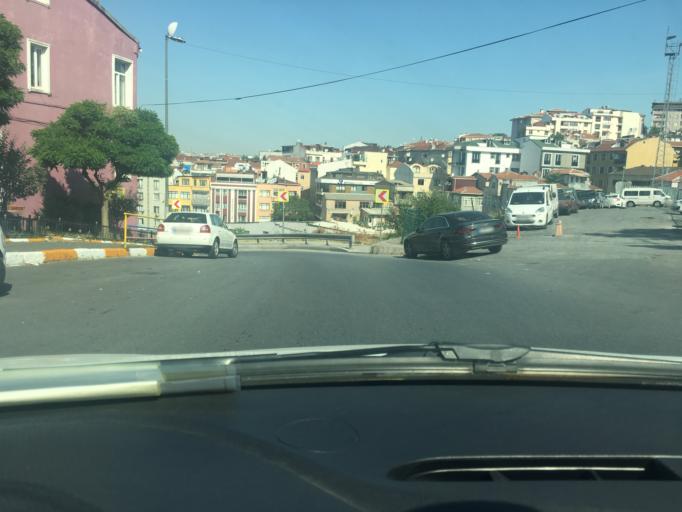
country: TR
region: Istanbul
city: Istanbul
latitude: 41.0392
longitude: 28.9552
